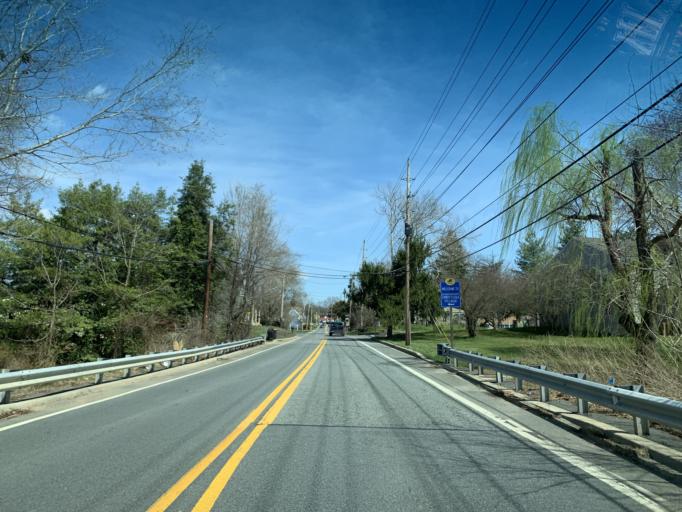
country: US
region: Delaware
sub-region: New Castle County
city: Bear
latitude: 39.6633
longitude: -75.6630
